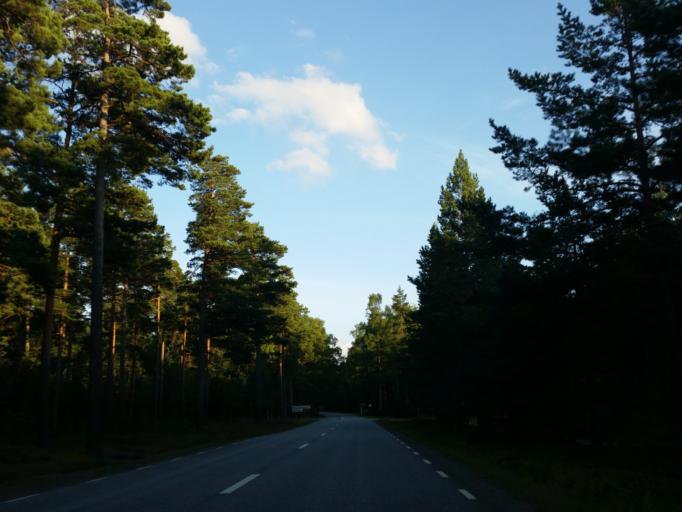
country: SE
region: Stockholm
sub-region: Sodertalje Kommun
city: Soedertaelje
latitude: 59.2348
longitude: 17.5469
